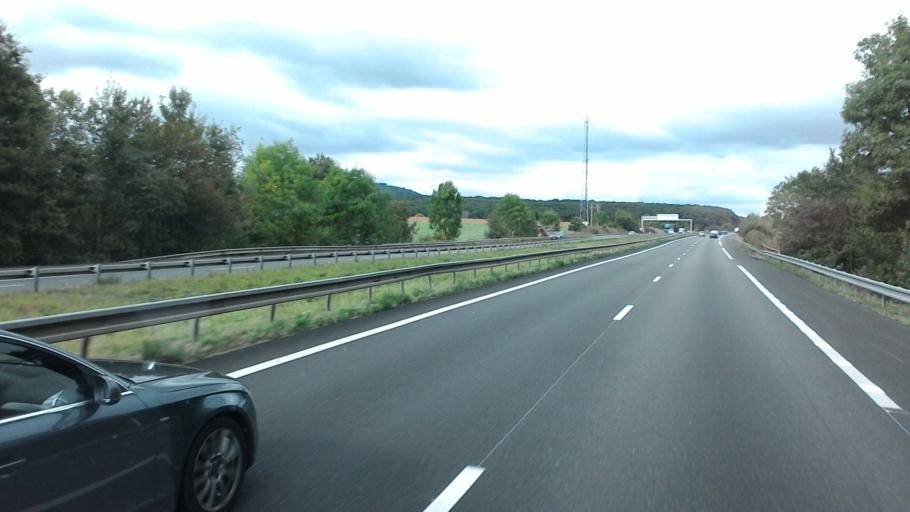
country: FR
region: Lorraine
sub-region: Departement de la Moselle
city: Noveant-sur-Moselle
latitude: 48.9737
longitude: 6.1045
